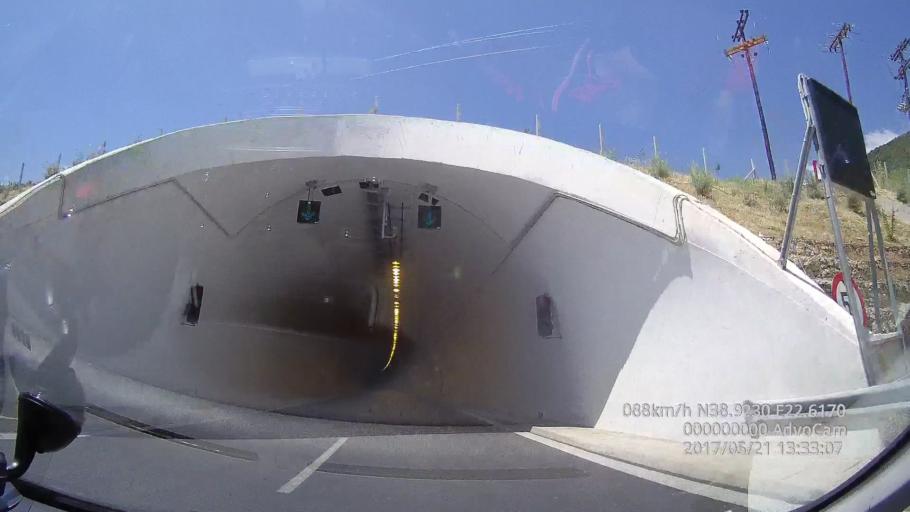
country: GR
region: Central Greece
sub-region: Nomos Fthiotidos
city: Stylida
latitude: 38.9230
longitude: 22.6167
